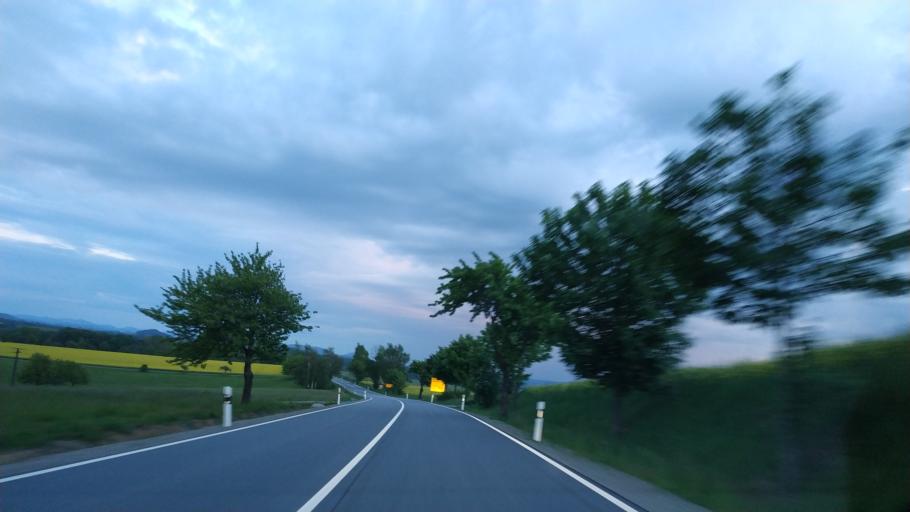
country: DE
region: Saxony
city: Hohnstein
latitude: 50.9927
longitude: 14.0788
